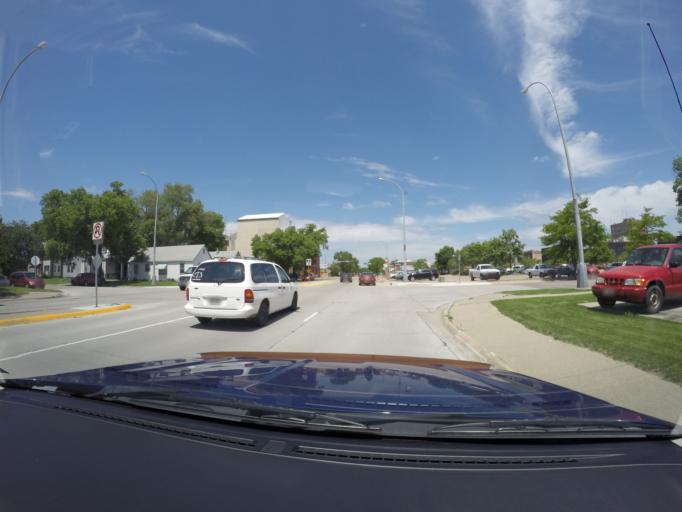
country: US
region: Nebraska
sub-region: Hall County
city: Grand Island
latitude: 40.9218
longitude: -98.3412
